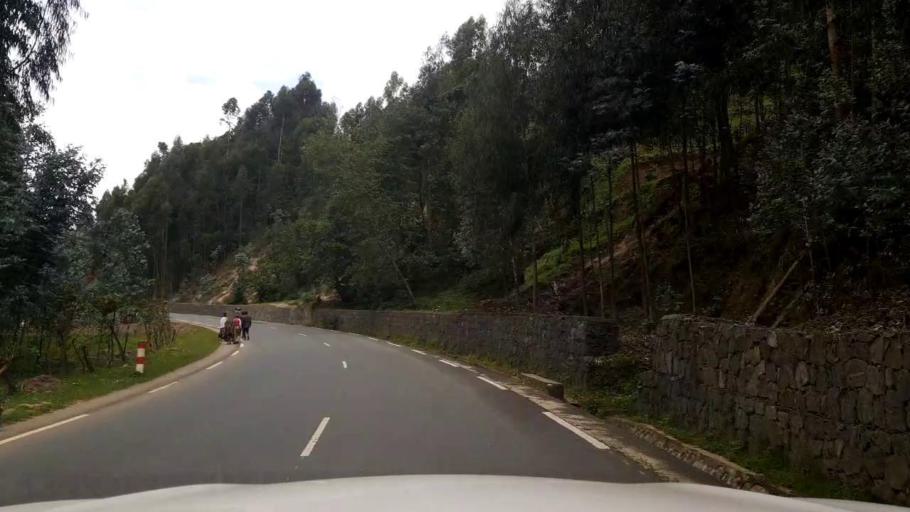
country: RW
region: Northern Province
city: Musanze
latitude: -1.6643
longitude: 29.5143
